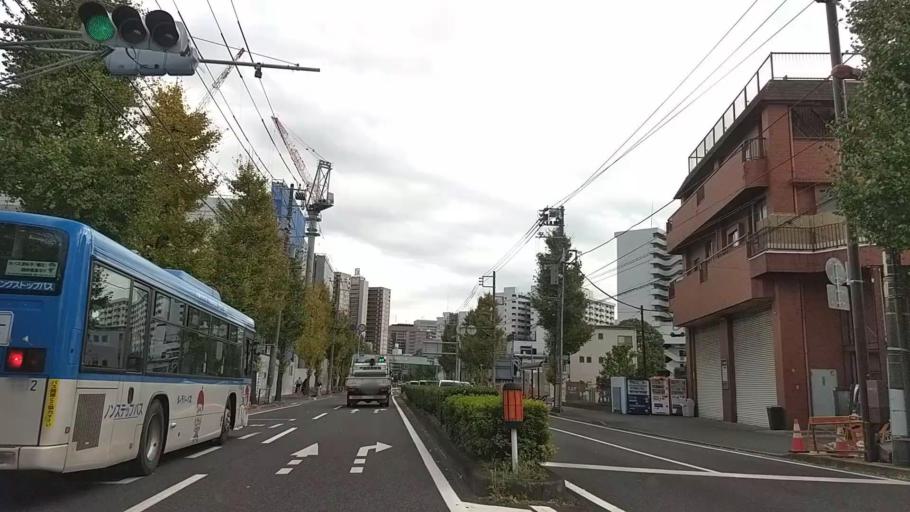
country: JP
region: Kanagawa
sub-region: Kawasaki-shi
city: Kawasaki
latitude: 35.5429
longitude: 139.6939
